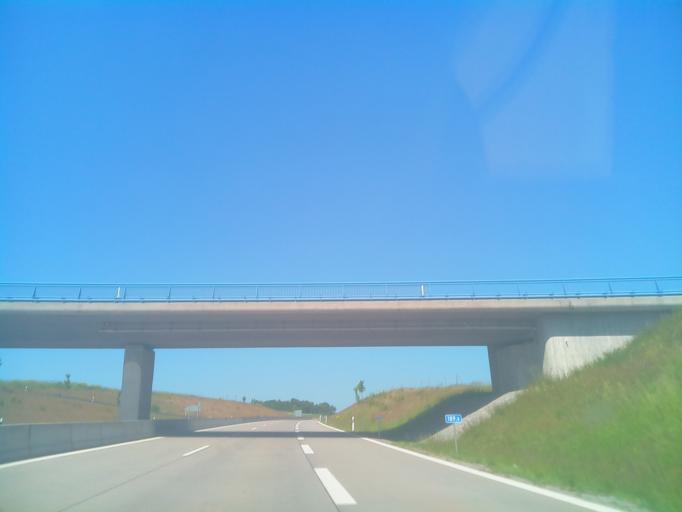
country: DE
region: Bavaria
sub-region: Regierungsbezirk Unterfranken
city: Munnerstadt
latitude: 50.2604
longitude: 10.2186
